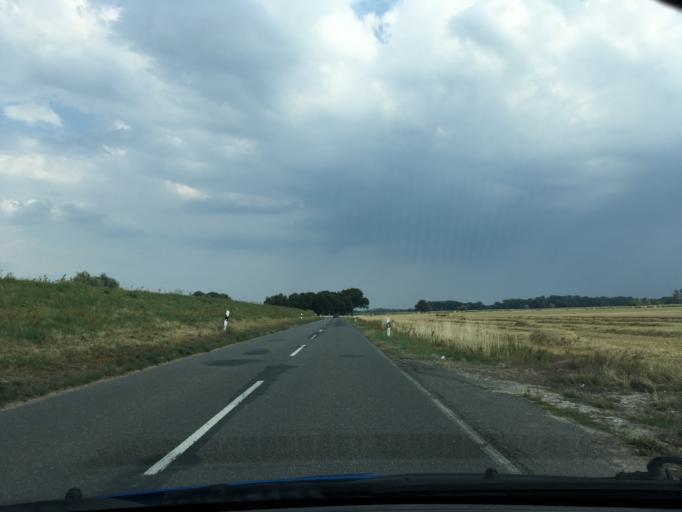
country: DE
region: Lower Saxony
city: Dannenberg
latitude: 53.1358
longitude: 11.0843
